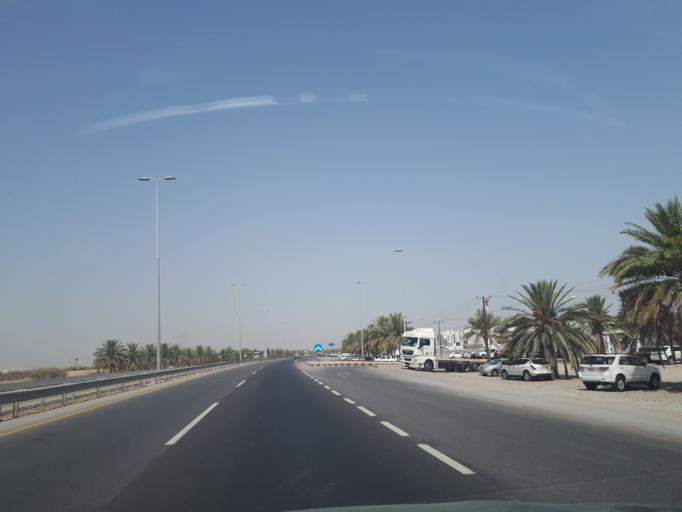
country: OM
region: Muhafazat Masqat
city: As Sib al Jadidah
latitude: 23.5892
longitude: 58.2251
